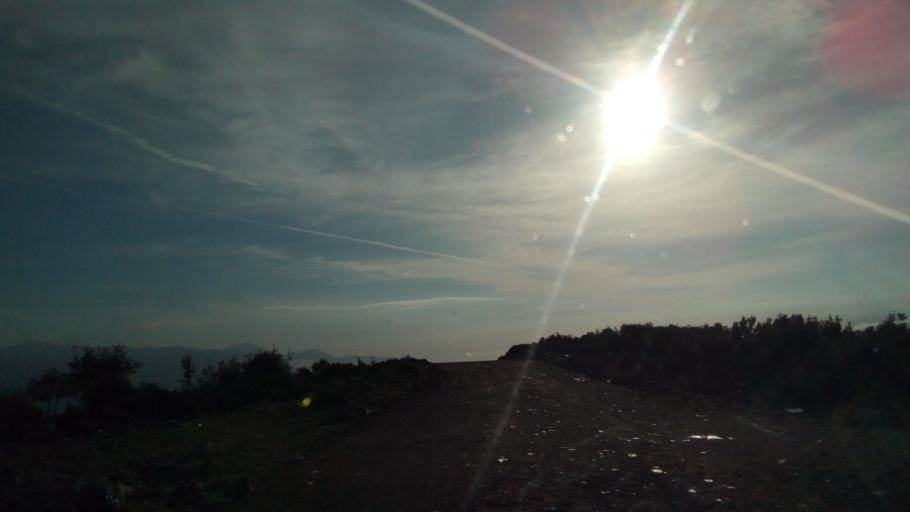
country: GR
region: West Greece
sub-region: Nomos Aitolias kai Akarnanias
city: Nafpaktos
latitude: 38.4150
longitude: 21.8155
